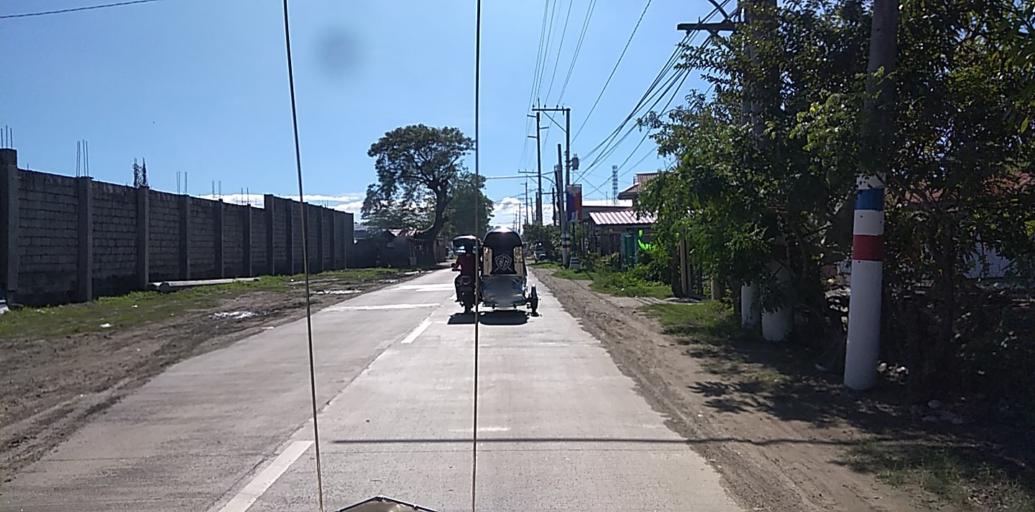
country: PH
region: Central Luzon
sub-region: Province of Pampanga
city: San Luis
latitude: 15.0497
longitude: 120.7832
